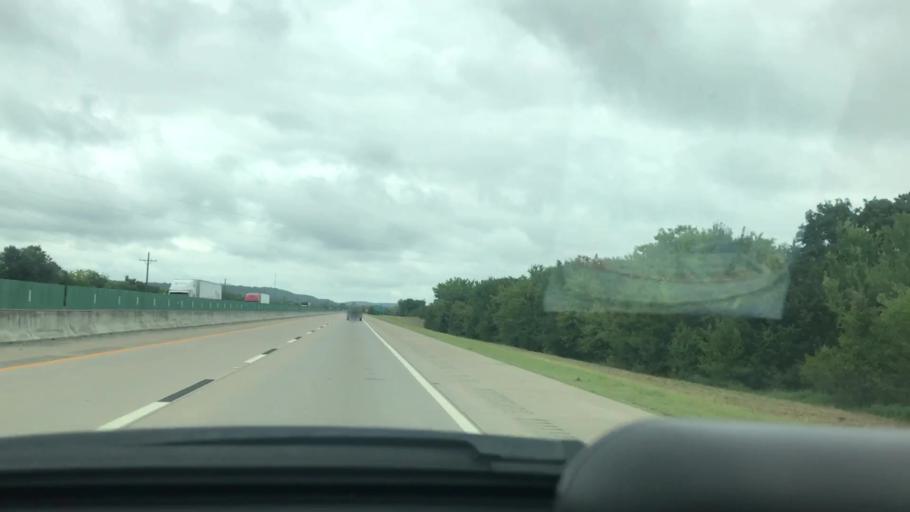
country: US
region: Oklahoma
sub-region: Pittsburg County
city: Krebs
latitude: 35.0358
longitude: -95.7124
